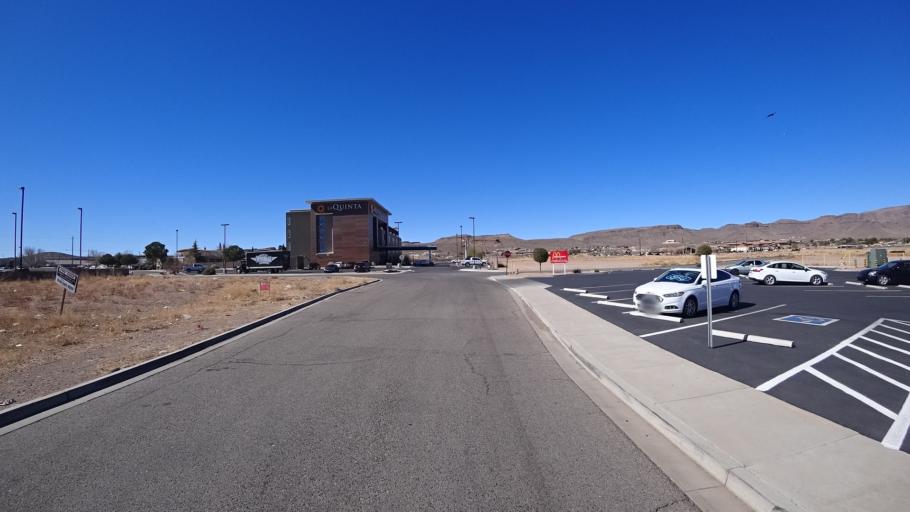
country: US
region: Arizona
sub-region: Mohave County
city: Kingman
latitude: 35.2234
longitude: -114.0373
